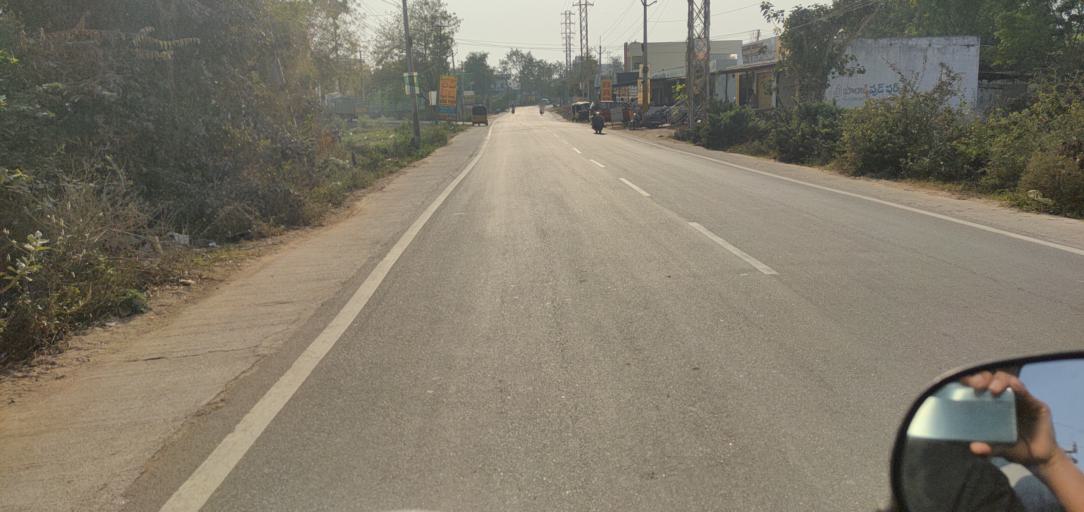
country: IN
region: Telangana
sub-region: Rangareddi
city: Lal Bahadur Nagar
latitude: 17.3378
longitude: 78.6188
